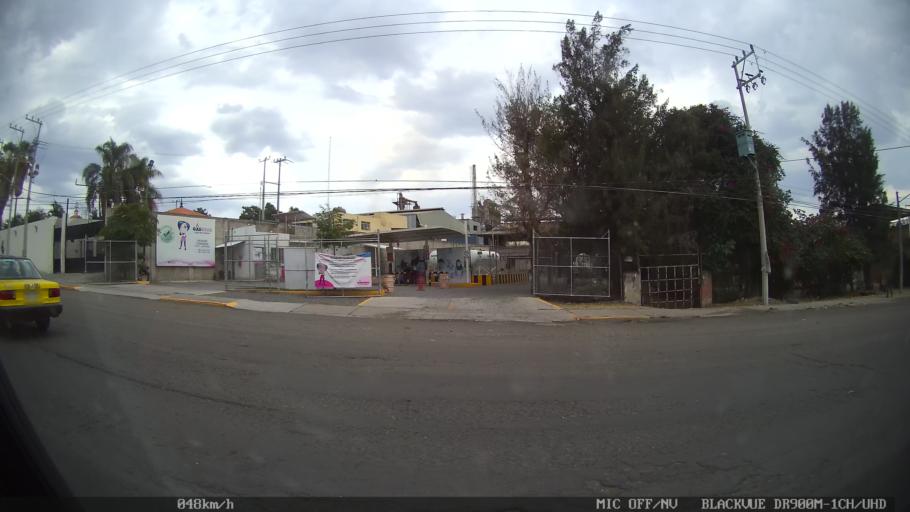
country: MX
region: Jalisco
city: Tlaquepaque
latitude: 20.6168
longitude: -103.2703
